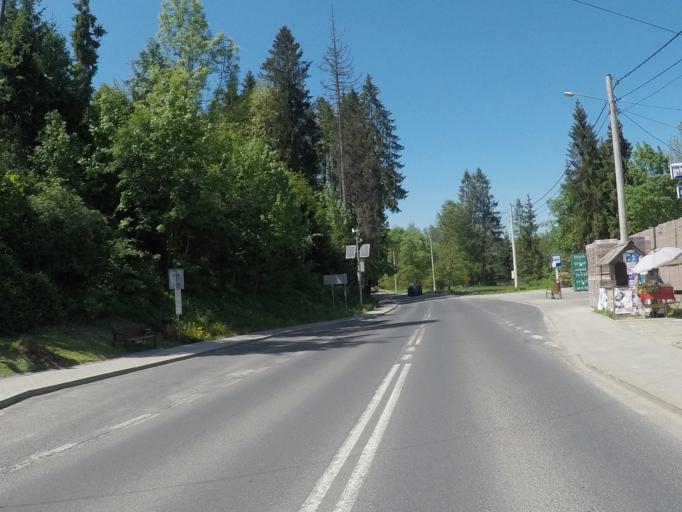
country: PL
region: Lesser Poland Voivodeship
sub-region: Powiat tatrzanski
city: Czarna Gora
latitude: 49.3578
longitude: 20.1240
